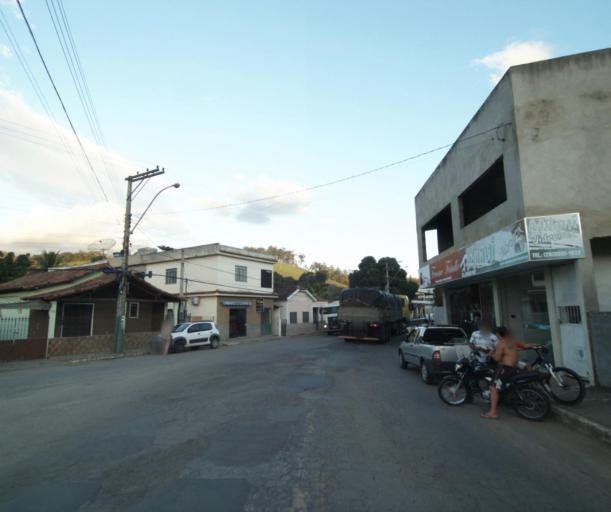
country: BR
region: Rio de Janeiro
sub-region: Bom Jesus Do Itabapoana
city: Bom Jesus do Itabapoana
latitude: -21.1513
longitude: -41.5690
